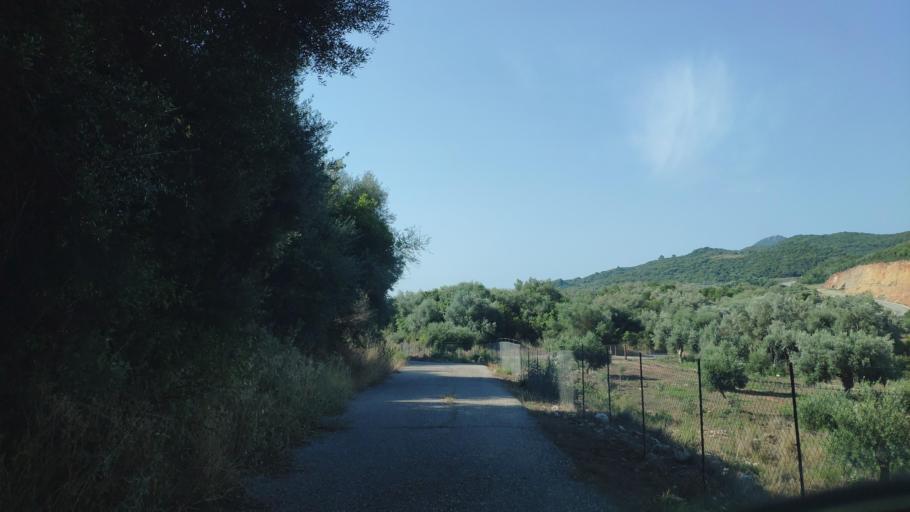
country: GR
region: West Greece
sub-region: Nomos Aitolias kai Akarnanias
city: Fitiai
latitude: 38.6976
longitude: 21.2097
